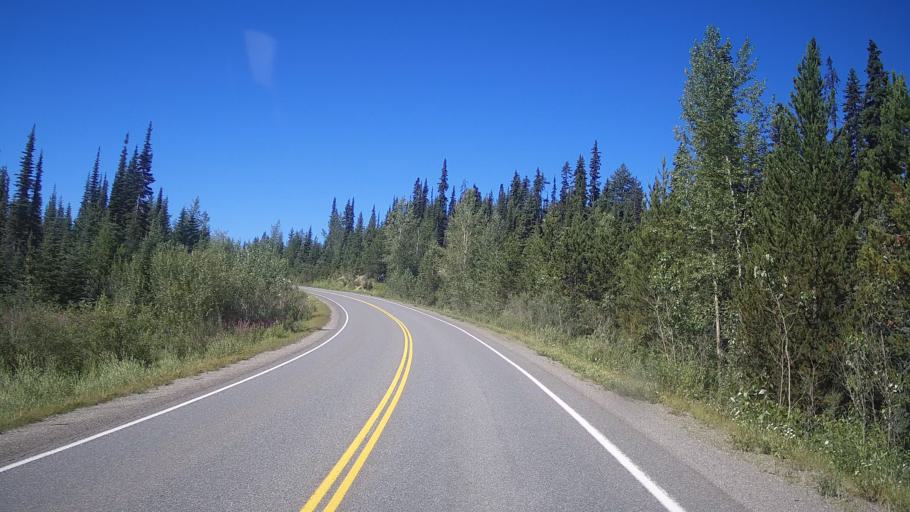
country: CA
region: British Columbia
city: Kamloops
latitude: 51.5036
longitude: -120.3551
